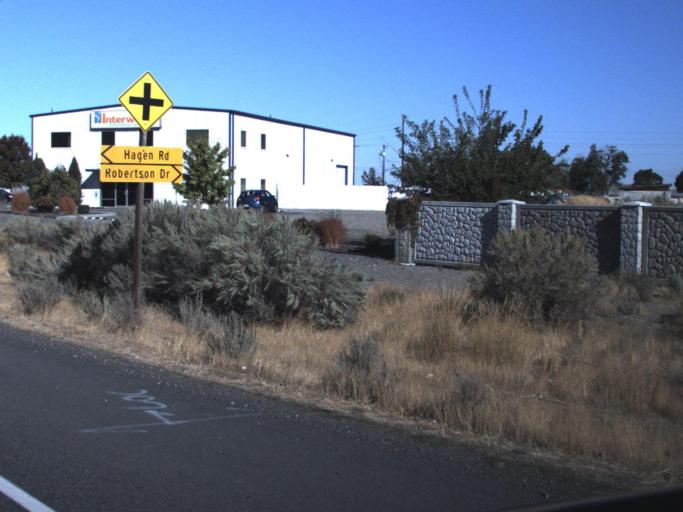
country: US
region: Washington
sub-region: Benton County
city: Richland
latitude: 46.3131
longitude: -119.2916
